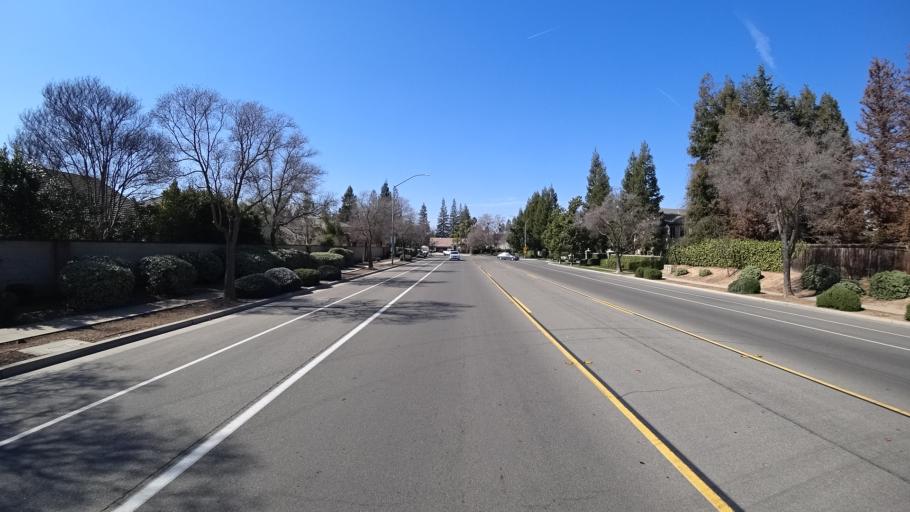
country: US
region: California
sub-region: Fresno County
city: Clovis
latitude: 36.8811
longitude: -119.7542
